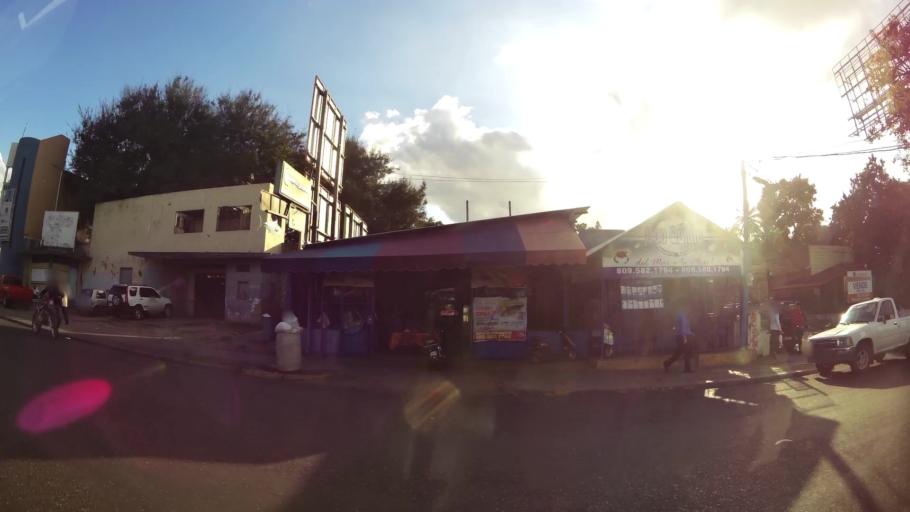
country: DO
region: Santiago
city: Santiago de los Caballeros
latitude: 19.4584
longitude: -70.7096
